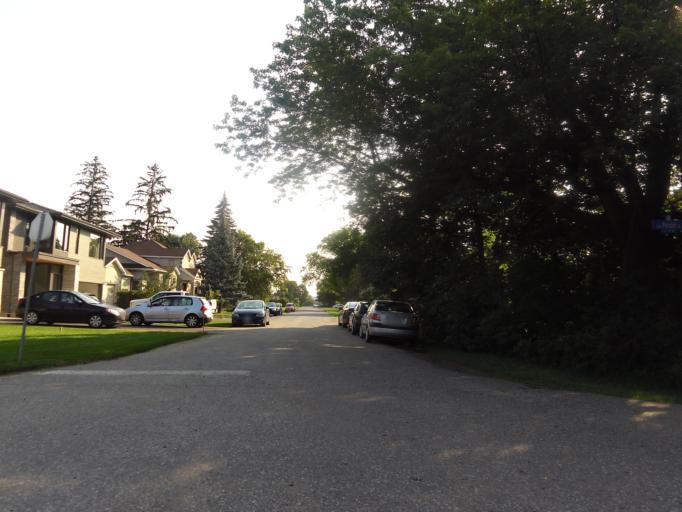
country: CA
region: Ontario
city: Ottawa
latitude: 45.3578
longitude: -75.7441
